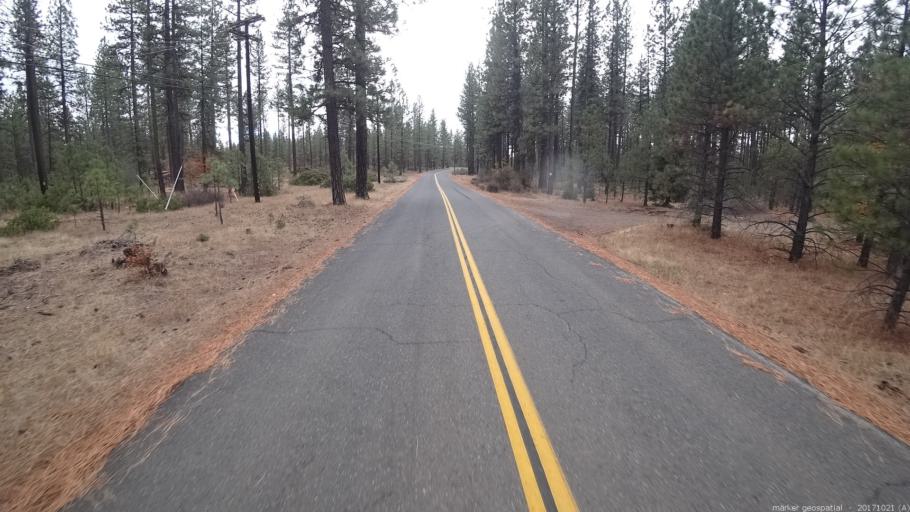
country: US
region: California
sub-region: Shasta County
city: Burney
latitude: 40.9321
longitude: -121.6431
